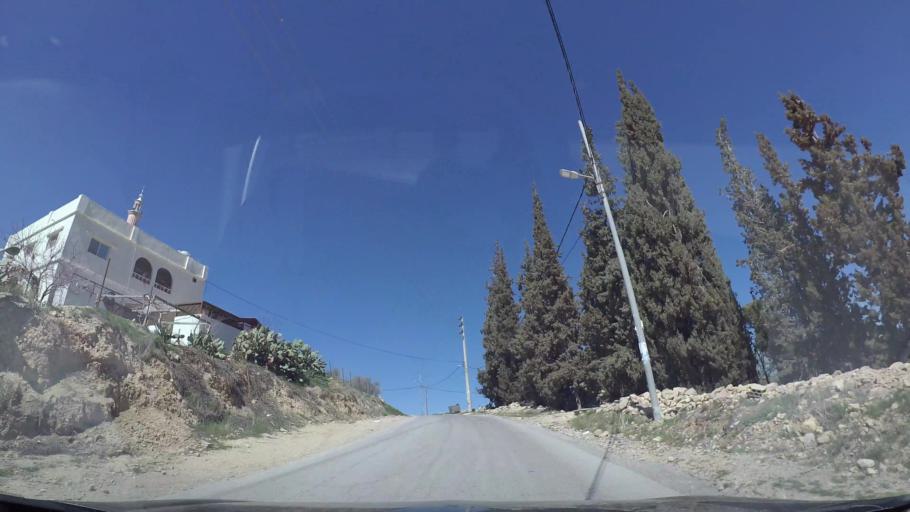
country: JO
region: Tafielah
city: At Tafilah
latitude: 30.8198
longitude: 35.5839
